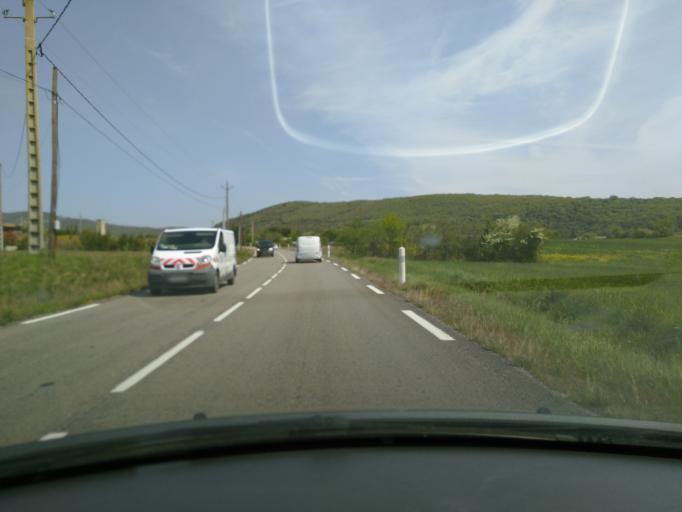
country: FR
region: Rhone-Alpes
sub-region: Departement de l'Ardeche
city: Alba-la-Romaine
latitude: 44.5677
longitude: 4.6081
